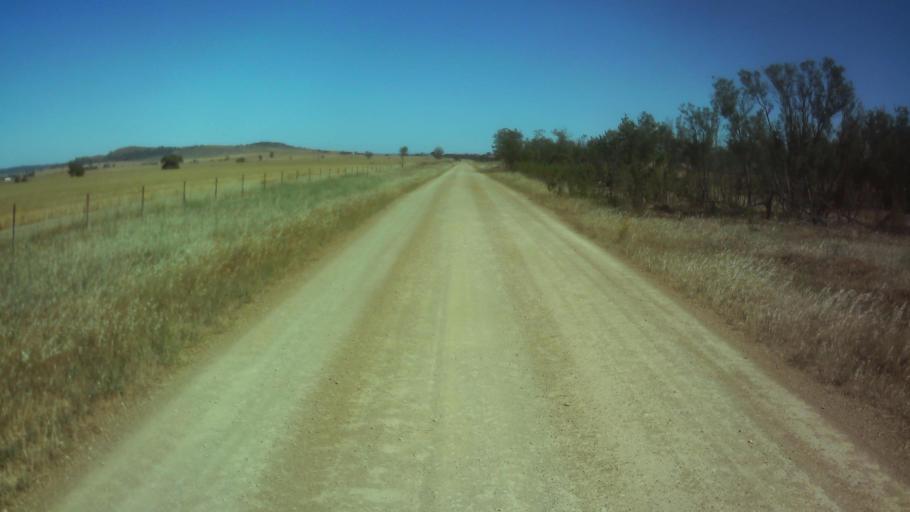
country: AU
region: New South Wales
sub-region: Weddin
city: Grenfell
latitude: -33.9811
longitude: 148.3286
